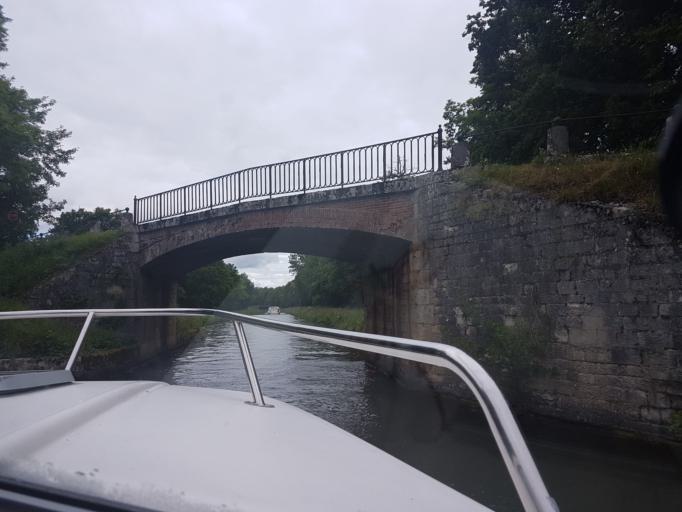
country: FR
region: Bourgogne
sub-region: Departement de l'Yonne
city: Vermenton
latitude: 47.6506
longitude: 3.6685
